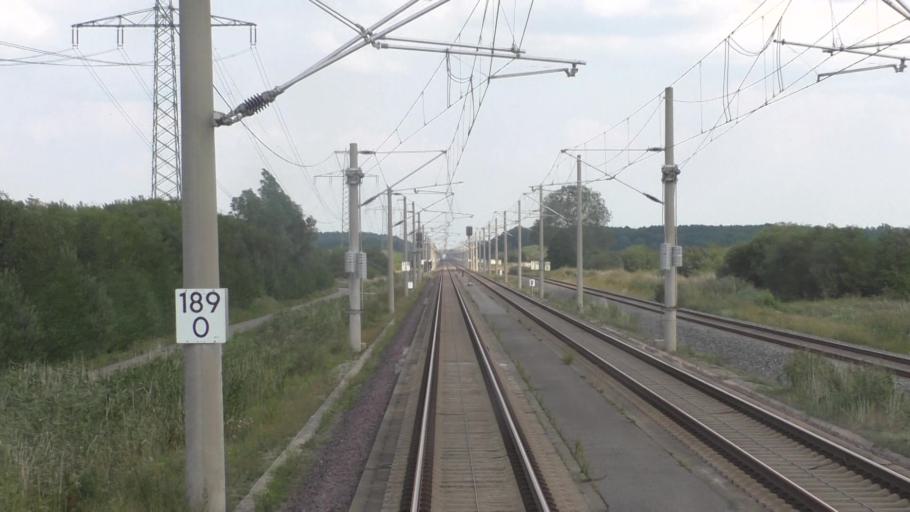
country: DE
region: Saxony-Anhalt
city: Schonhausen
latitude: 52.5905
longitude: 12.0888
